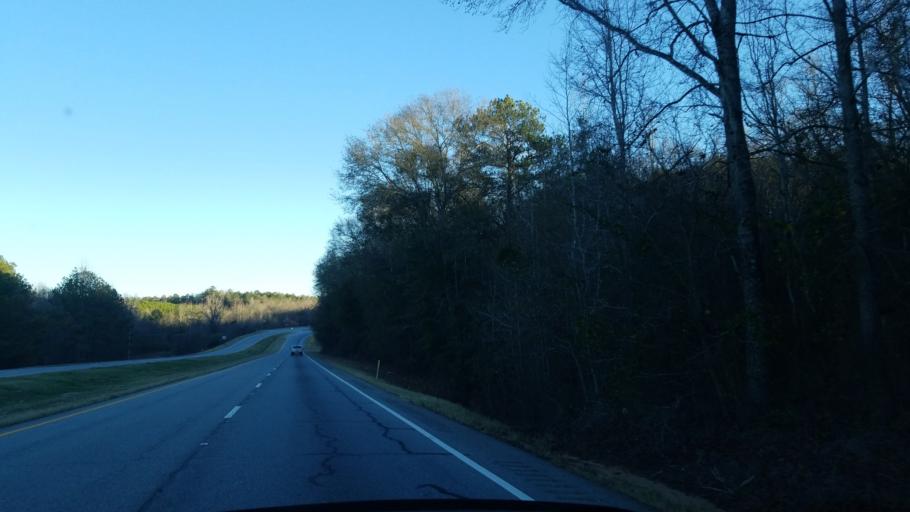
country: US
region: Georgia
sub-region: Chattahoochee County
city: Cusseta
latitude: 32.2609
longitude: -84.7308
